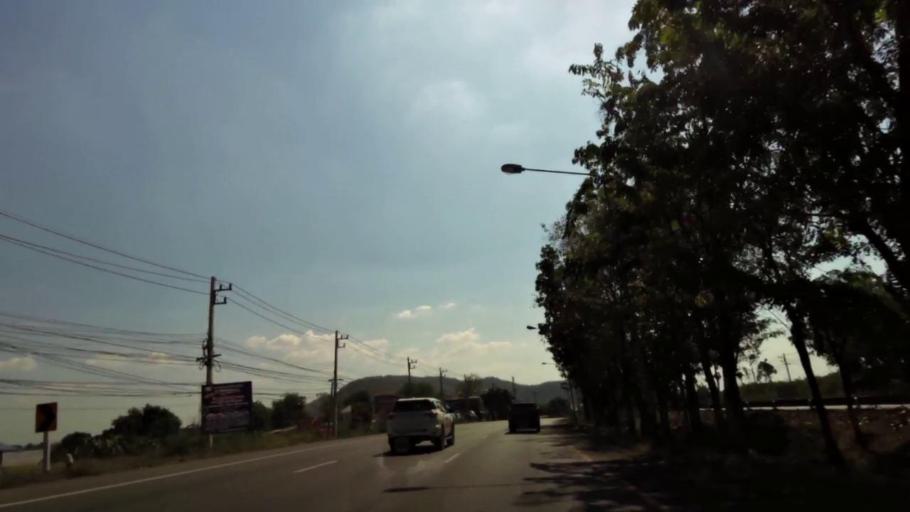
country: TH
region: Nakhon Sawan
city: Nakhon Sawan
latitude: 15.6437
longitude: 100.1348
